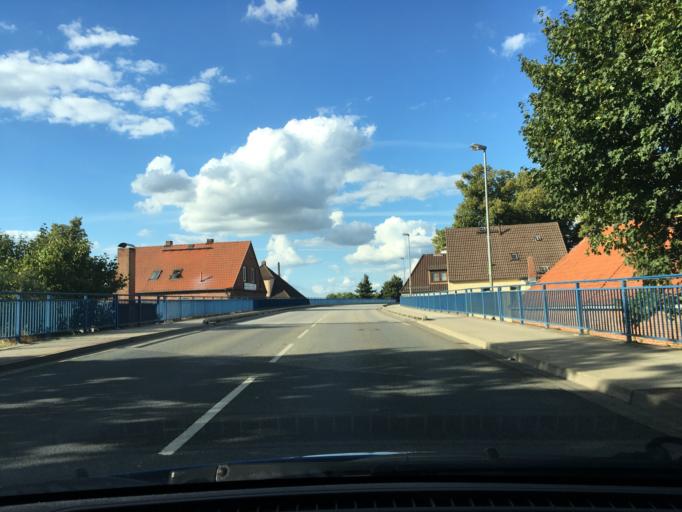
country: DE
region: Mecklenburg-Vorpommern
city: Ludwigslust
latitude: 53.3284
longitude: 11.5016
